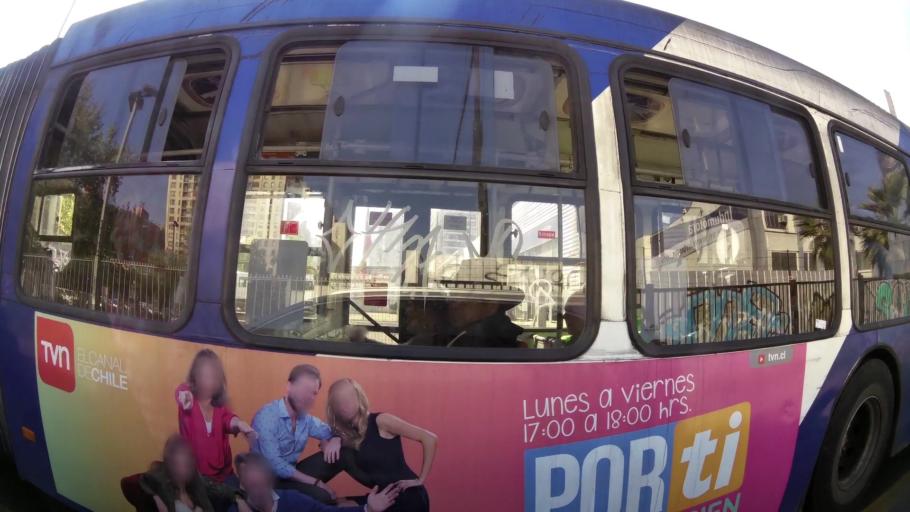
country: CL
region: Santiago Metropolitan
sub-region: Provincia de Santiago
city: Santiago
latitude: -33.4506
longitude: -70.6444
